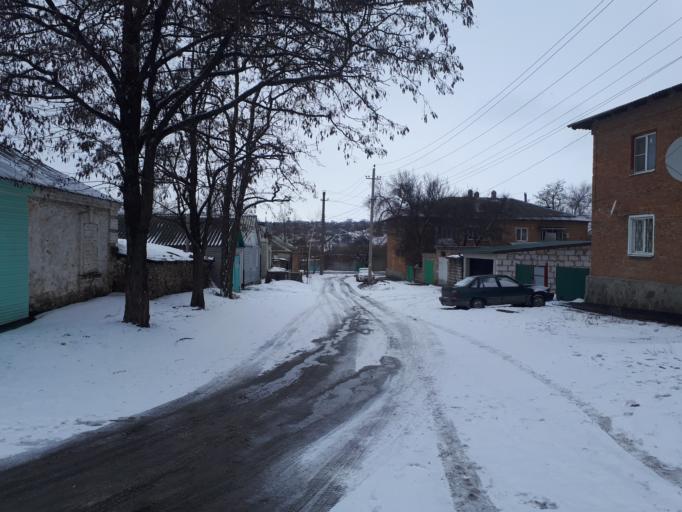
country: RU
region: Rostov
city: Krasnyy Sulin
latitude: 47.8993
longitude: 40.0551
